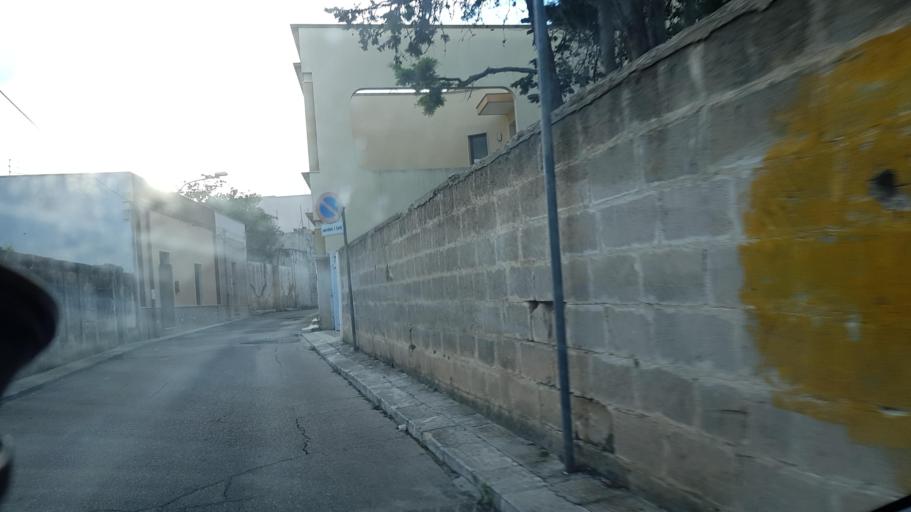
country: IT
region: Apulia
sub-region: Provincia di Brindisi
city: San Vito dei Normanni
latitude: 40.6605
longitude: 17.7066
